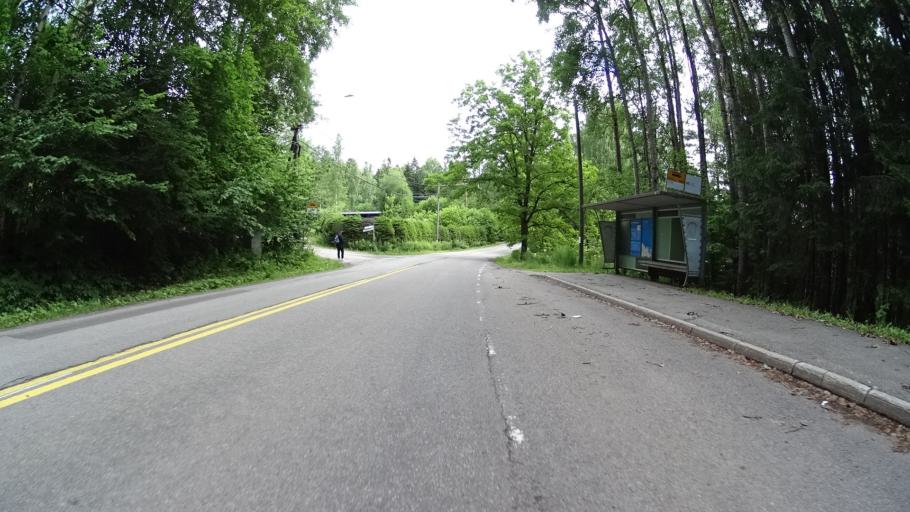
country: FI
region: Uusimaa
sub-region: Helsinki
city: Espoo
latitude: 60.2620
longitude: 24.6529
